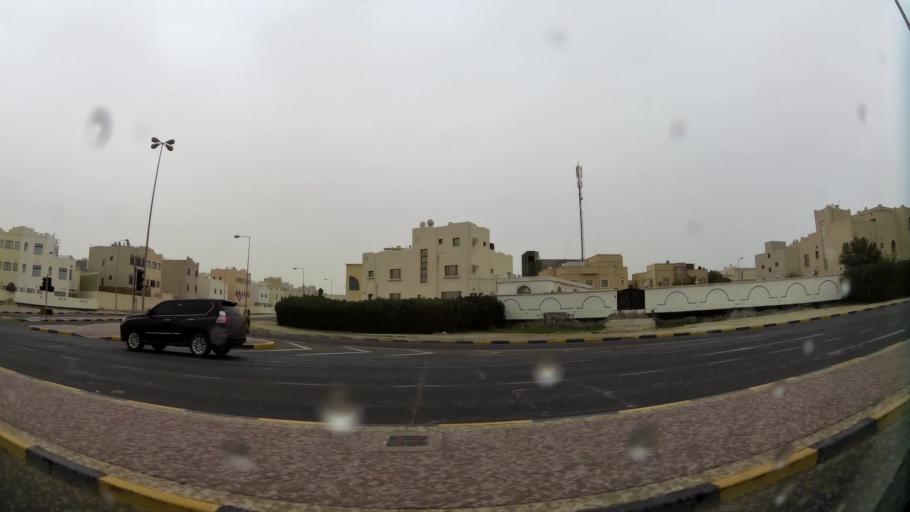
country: BH
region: Northern
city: Madinat `Isa
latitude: 26.1561
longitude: 50.5739
